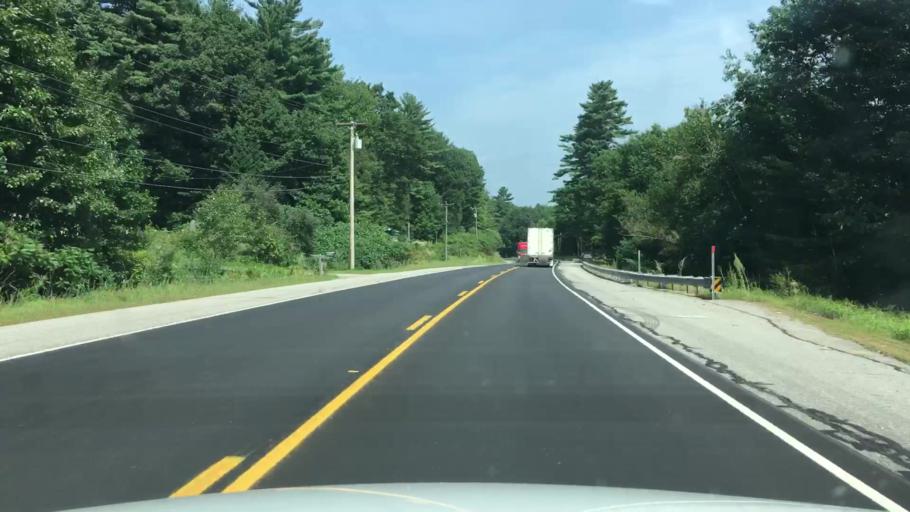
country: US
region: Maine
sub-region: Androscoggin County
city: Turner
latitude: 44.3020
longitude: -70.2688
